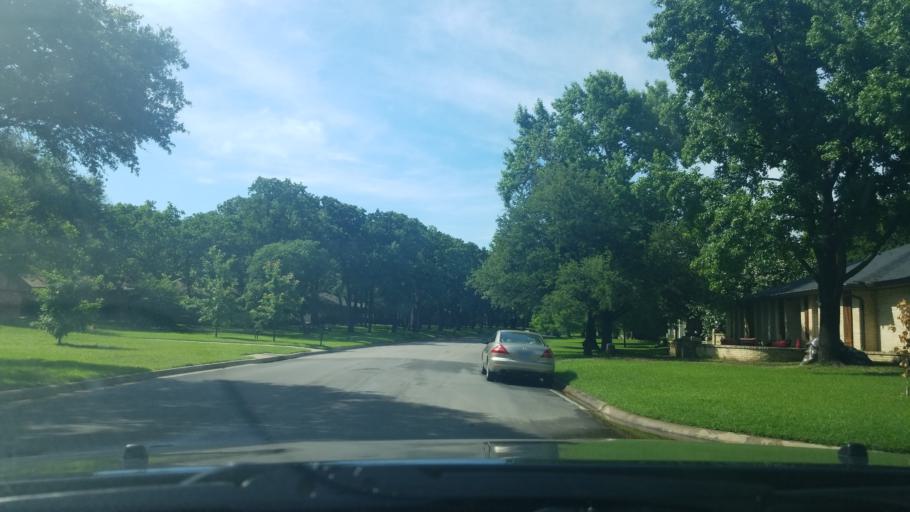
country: US
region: Texas
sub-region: Denton County
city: Denton
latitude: 33.1844
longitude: -97.1192
